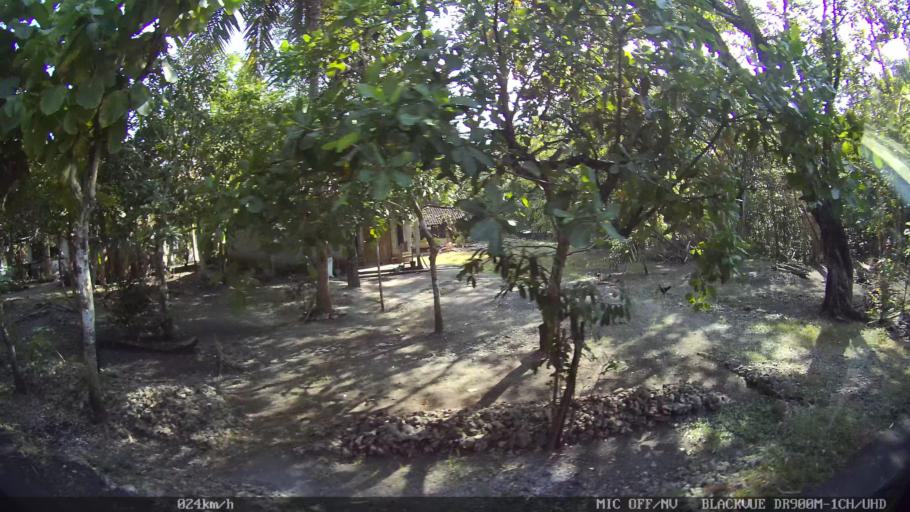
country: ID
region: Daerah Istimewa Yogyakarta
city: Kasihan
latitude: -7.8245
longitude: 110.2902
